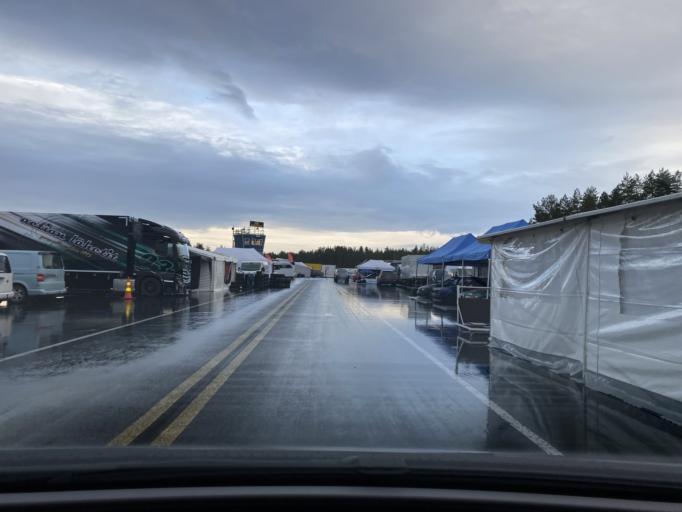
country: FI
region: Satakunta
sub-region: Pori
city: Vampula
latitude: 60.9734
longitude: 22.6584
